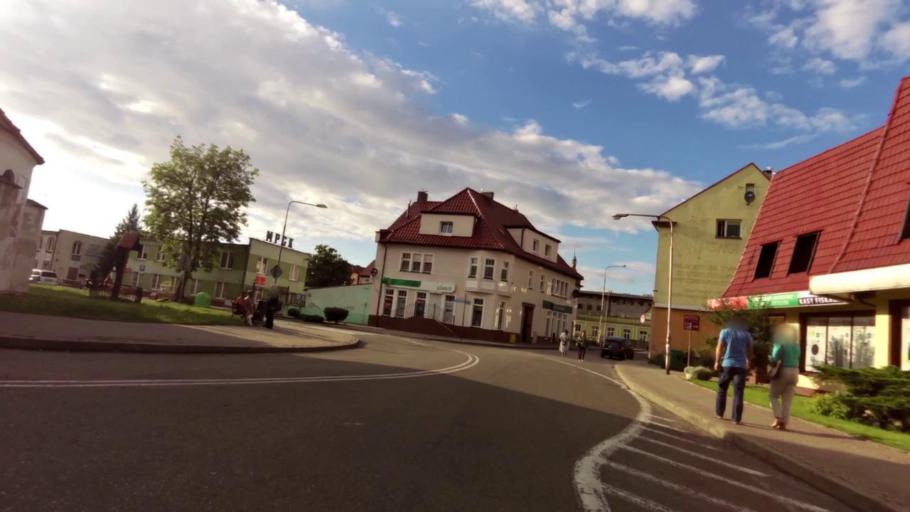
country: PL
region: West Pomeranian Voivodeship
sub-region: Powiat slawienski
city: Darlowo
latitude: 54.4191
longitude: 16.4091
